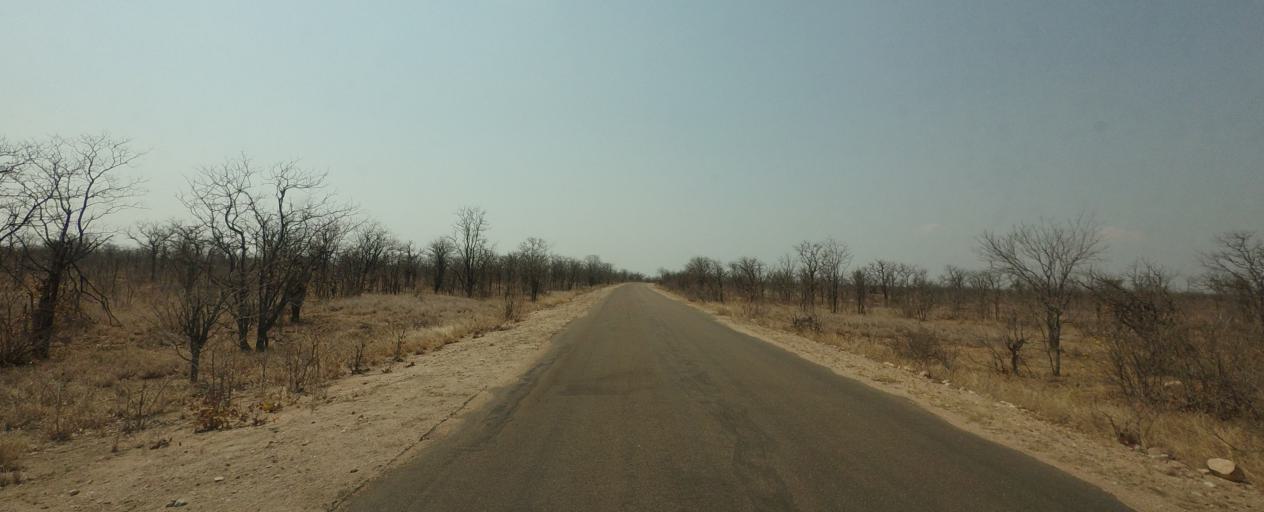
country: ZA
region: Limpopo
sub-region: Mopani District Municipality
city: Giyani
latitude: -23.3546
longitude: 31.3189
